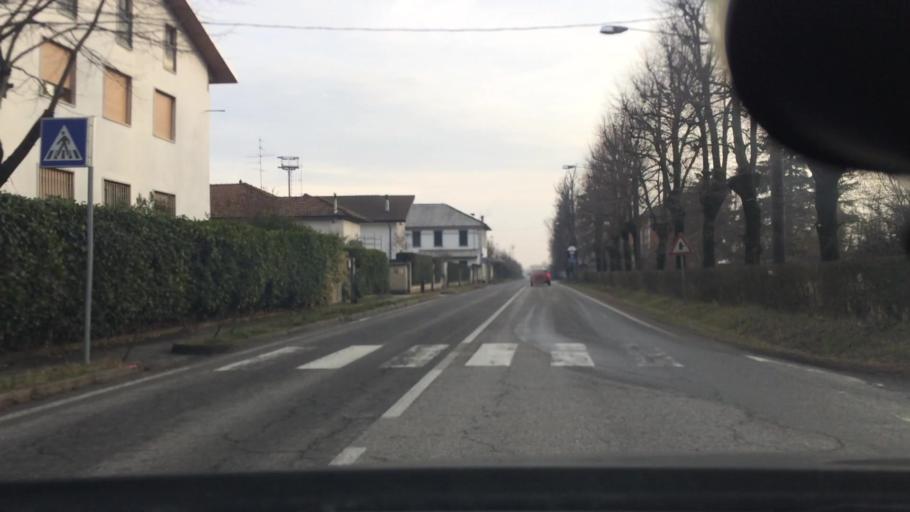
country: IT
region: Lombardy
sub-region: Provincia di Varese
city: Origgio
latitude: 45.5958
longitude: 9.0230
